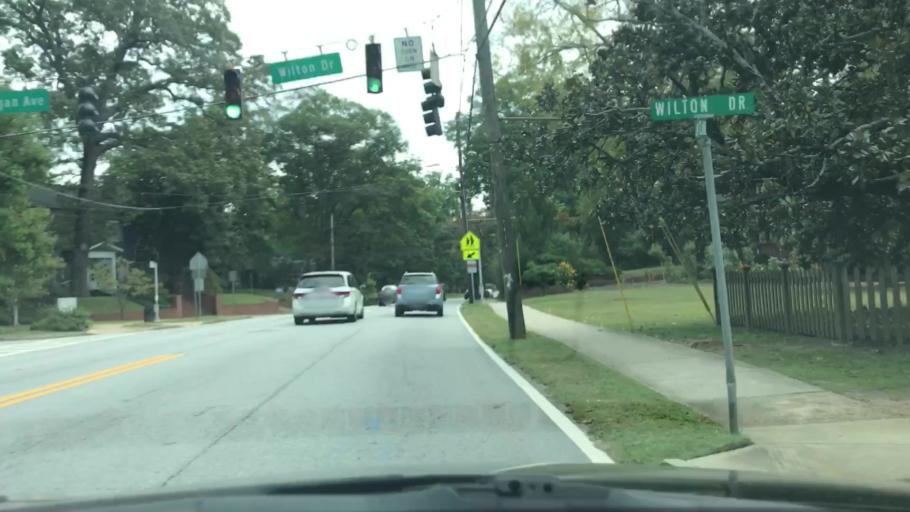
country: US
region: Georgia
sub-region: DeKalb County
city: Decatur
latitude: 33.7821
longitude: -84.2996
